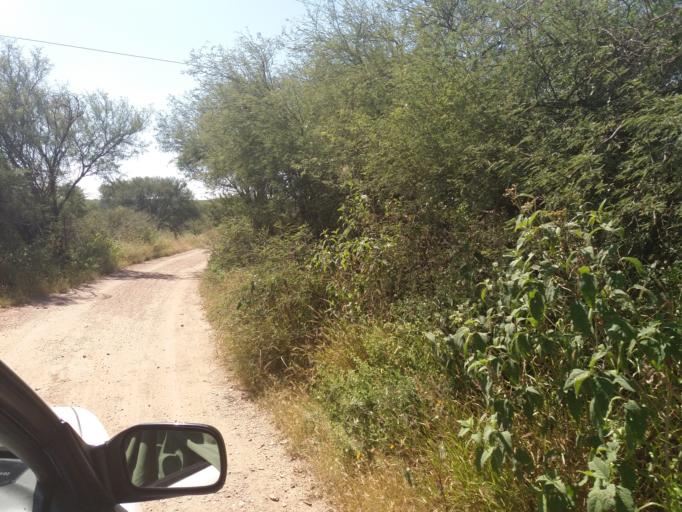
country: MX
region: Aguascalientes
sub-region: Aguascalientes
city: Penuelas (El Cienegal)
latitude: 21.7681
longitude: -102.2408
